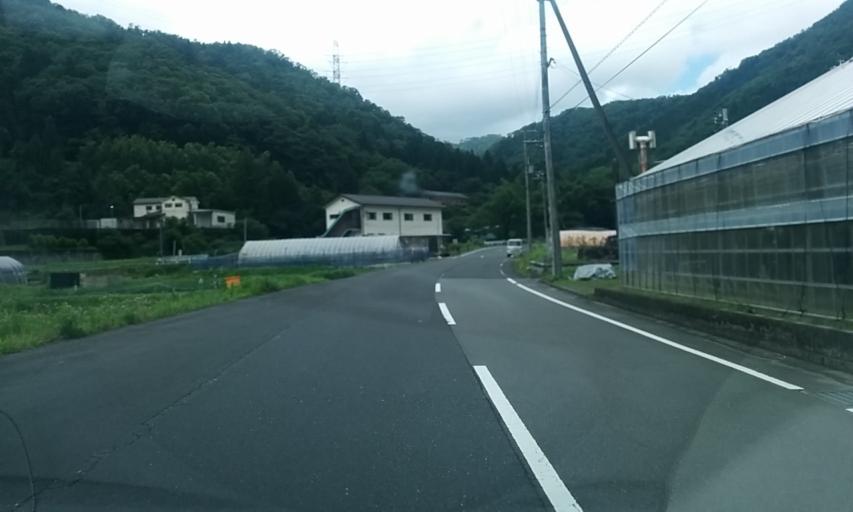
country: JP
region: Kyoto
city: Kameoka
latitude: 35.0610
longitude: 135.4298
